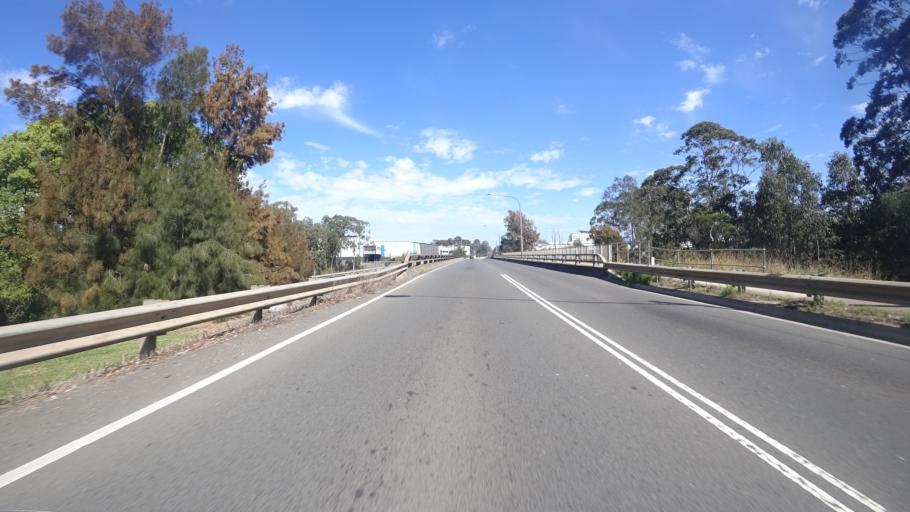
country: AU
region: New South Wales
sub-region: Fairfield
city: Chipping Norton
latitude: -33.9156
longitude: 150.9517
